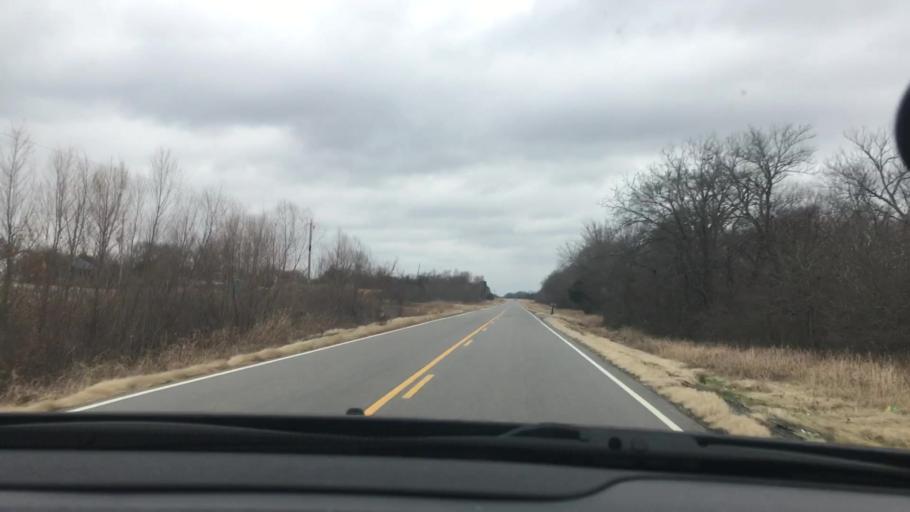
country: US
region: Oklahoma
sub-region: Atoka County
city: Atoka
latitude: 34.3749
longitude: -96.1638
